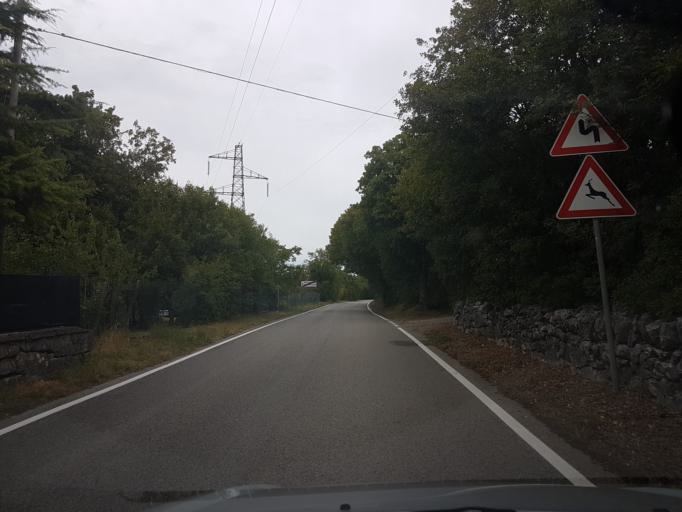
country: IT
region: Friuli Venezia Giulia
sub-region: Provincia di Trieste
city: Aurisina
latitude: 45.7577
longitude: 13.6886
